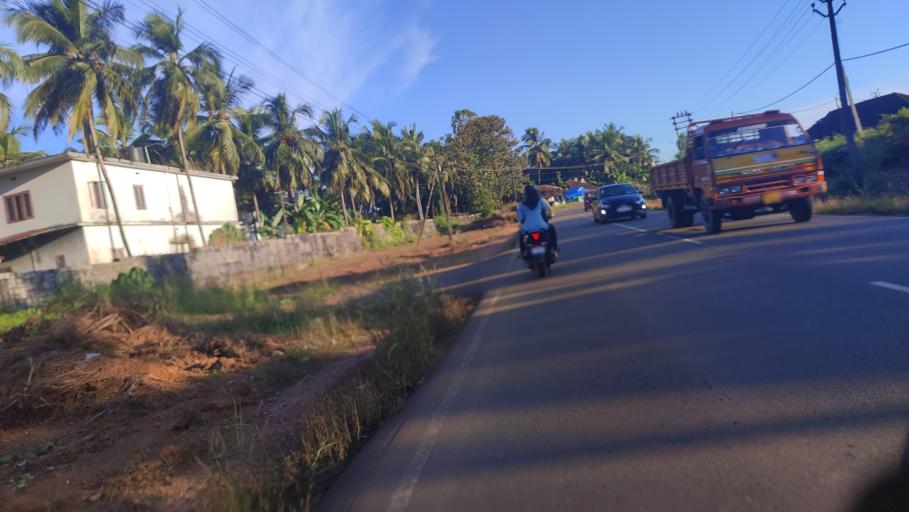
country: IN
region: Kerala
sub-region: Kasaragod District
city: Kasaragod
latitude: 12.4748
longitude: 75.0592
